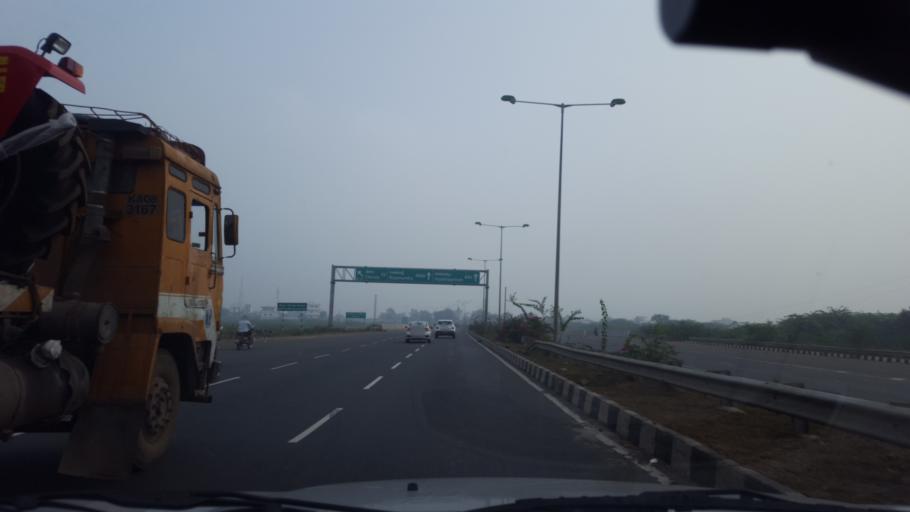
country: IN
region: Andhra Pradesh
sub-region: Prakasam
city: Ongole
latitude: 15.5468
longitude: 80.0542
